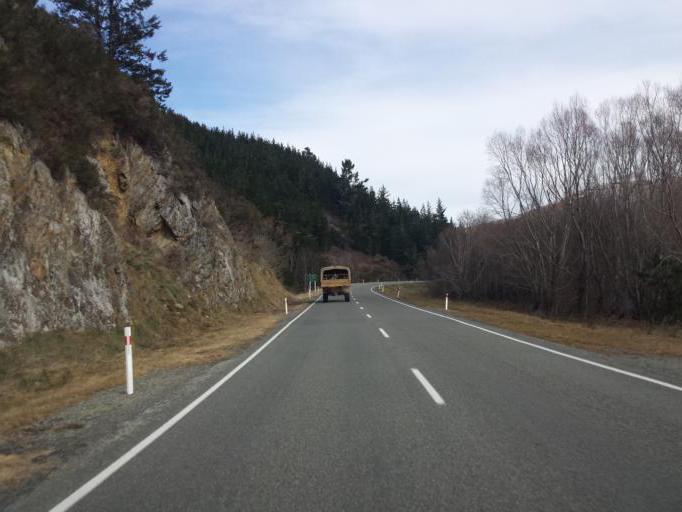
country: NZ
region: Canterbury
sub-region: Timaru District
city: Pleasant Point
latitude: -44.0303
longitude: 170.7111
